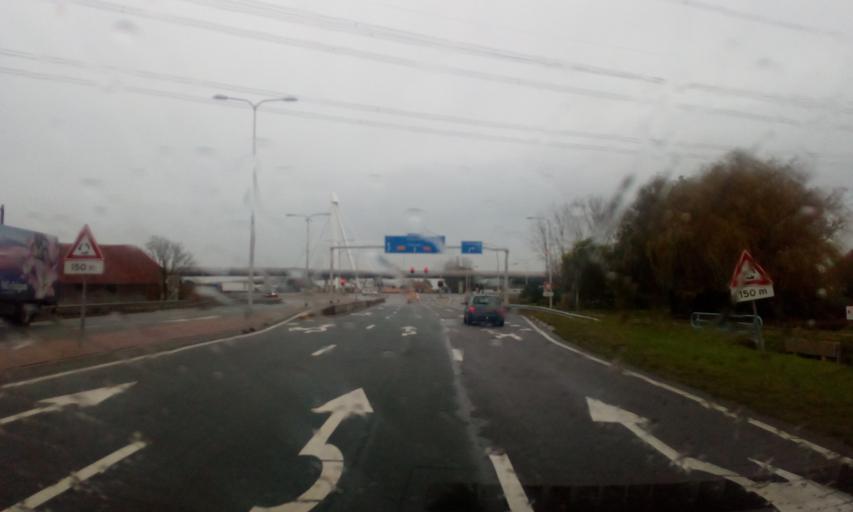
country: NL
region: South Holland
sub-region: Gemeente Westland
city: Naaldwijk
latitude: 51.9831
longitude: 4.2199
